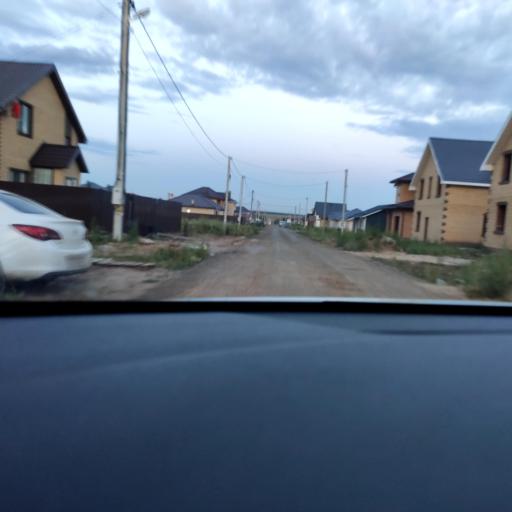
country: RU
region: Tatarstan
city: Stolbishchi
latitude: 55.7163
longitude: 49.3003
